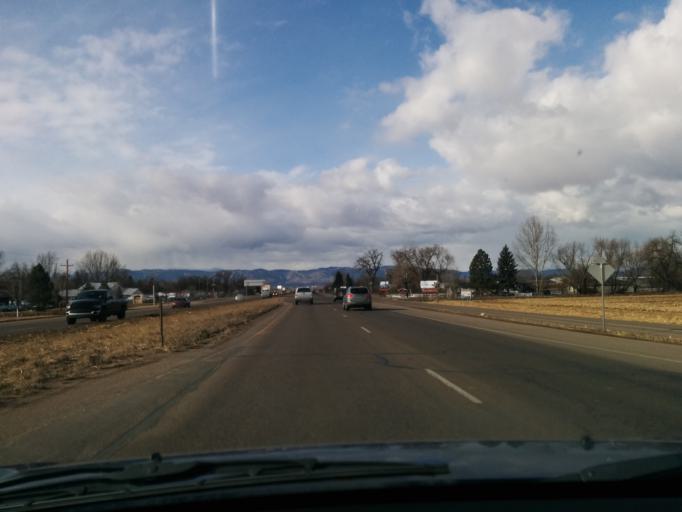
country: US
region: Colorado
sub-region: Larimer County
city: Fort Collins
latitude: 40.5812
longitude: -105.0160
